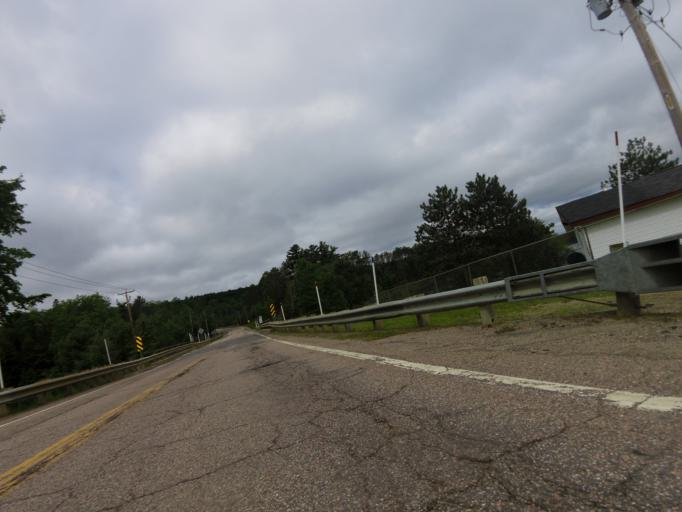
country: CA
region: Quebec
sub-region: Outaouais
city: Shawville
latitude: 45.8378
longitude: -76.4554
